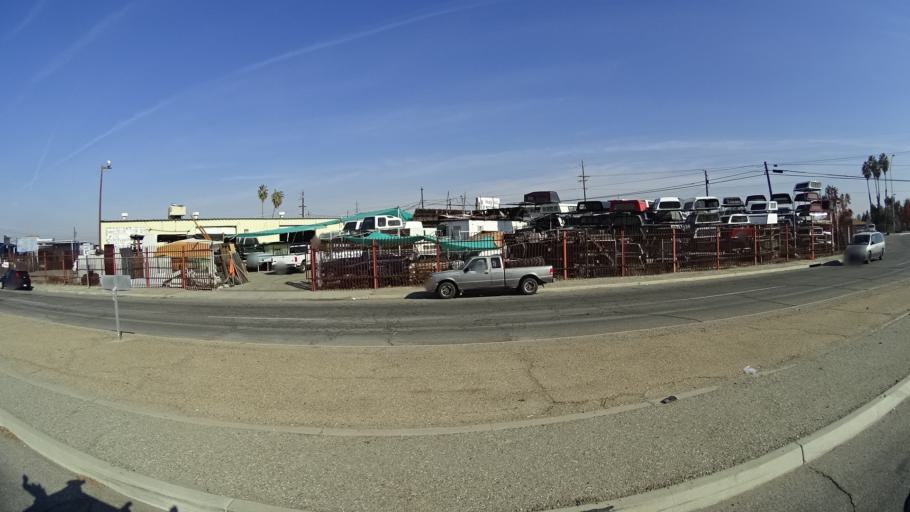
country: US
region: California
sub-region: Kern County
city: Greenfield
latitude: 35.3190
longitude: -119.0037
